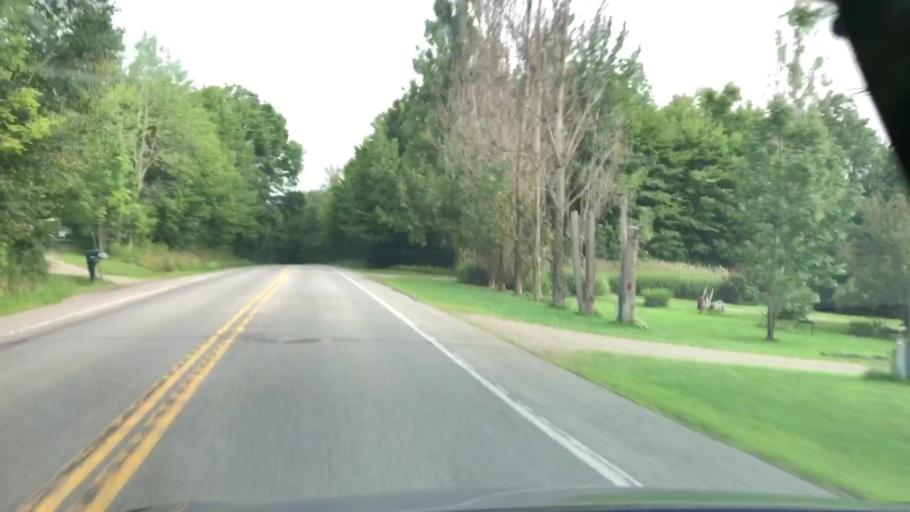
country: US
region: Pennsylvania
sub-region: Erie County
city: Union City
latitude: 41.8059
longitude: -79.7984
